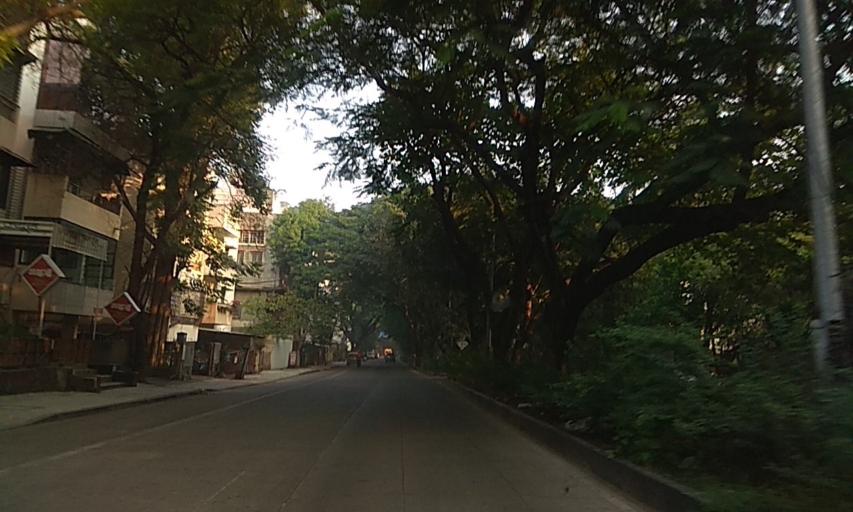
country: IN
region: Maharashtra
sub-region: Pune Division
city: Shivaji Nagar
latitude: 18.5439
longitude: 73.8172
